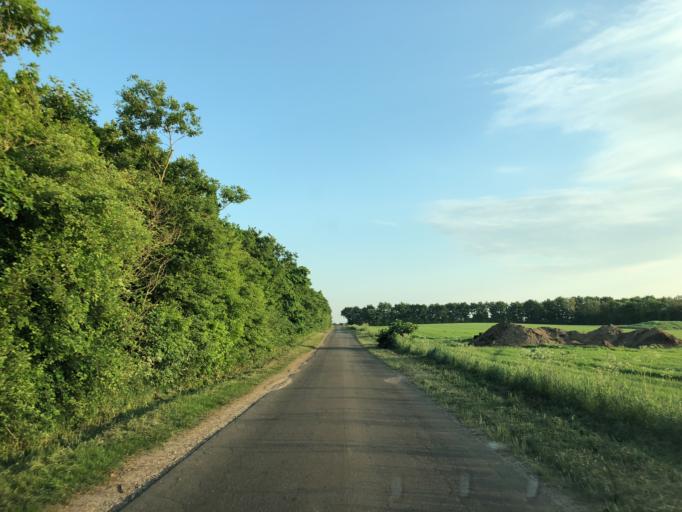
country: DK
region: Central Jutland
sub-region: Struer Kommune
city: Struer
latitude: 56.3991
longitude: 8.4848
